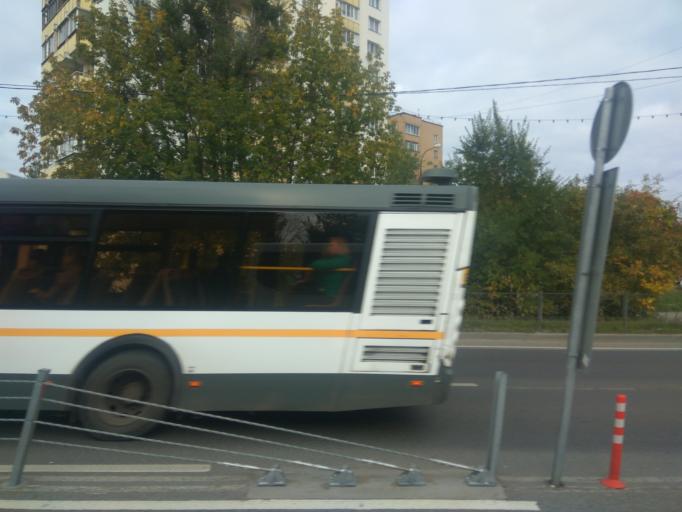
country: RU
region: Moskovskaya
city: Fryazino
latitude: 55.9540
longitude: 38.0549
